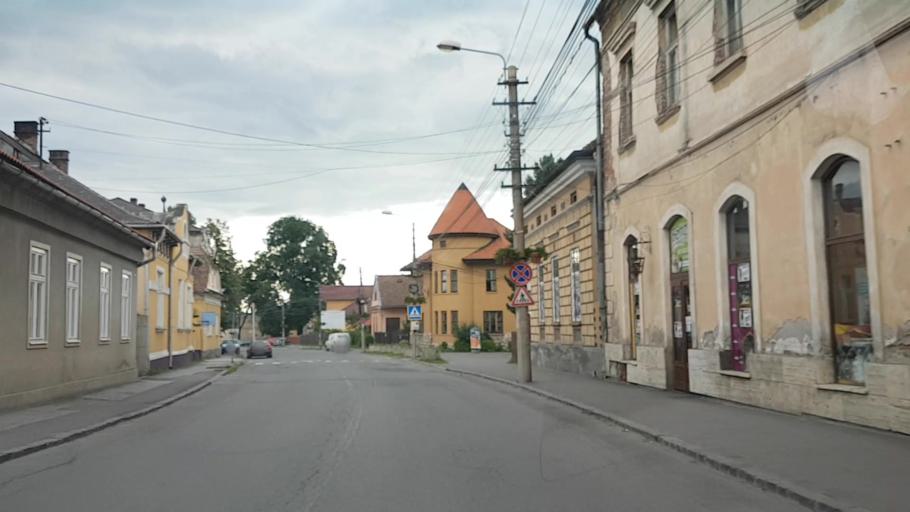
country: RO
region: Harghita
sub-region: Municipiul Gheorgheni
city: Gheorgheni
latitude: 46.7218
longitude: 25.5969
